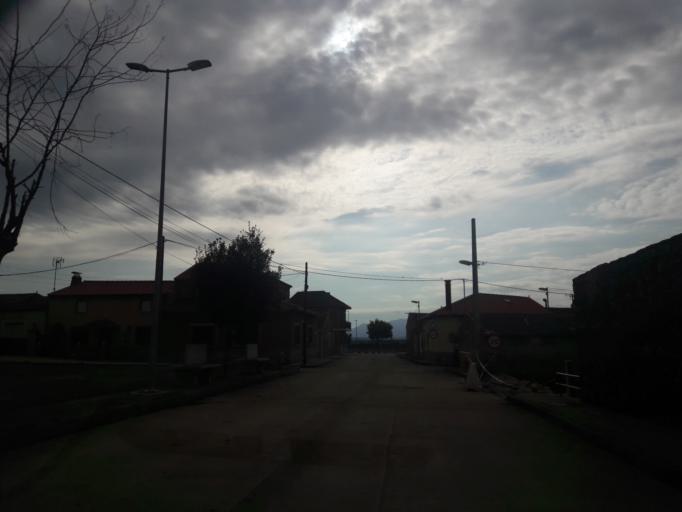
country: ES
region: Castille and Leon
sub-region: Provincia de Salamanca
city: Pastores
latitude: 40.4995
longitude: -6.5292
